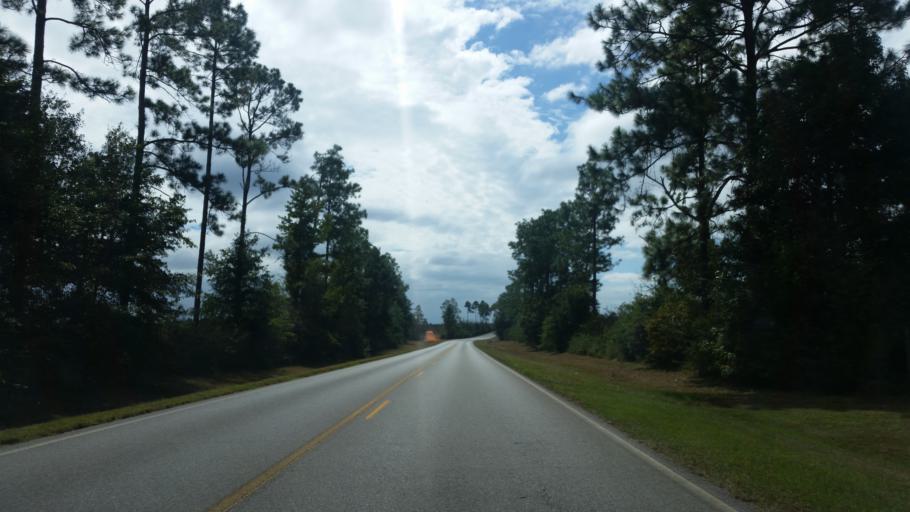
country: US
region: Florida
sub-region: Santa Rosa County
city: Point Baker
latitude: 30.7317
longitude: -86.9514
